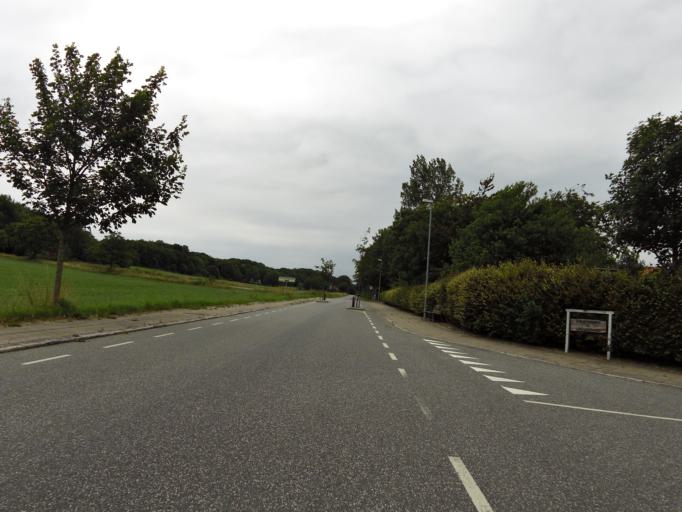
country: DK
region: South Denmark
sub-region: Tonder Kommune
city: Logumkloster
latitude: 55.0817
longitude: 8.9323
